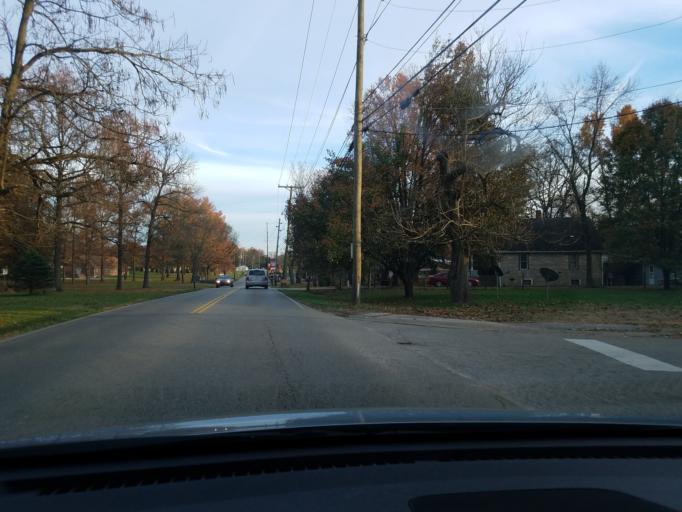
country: US
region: Indiana
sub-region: Clark County
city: Clarksville
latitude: 38.3322
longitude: -85.7923
